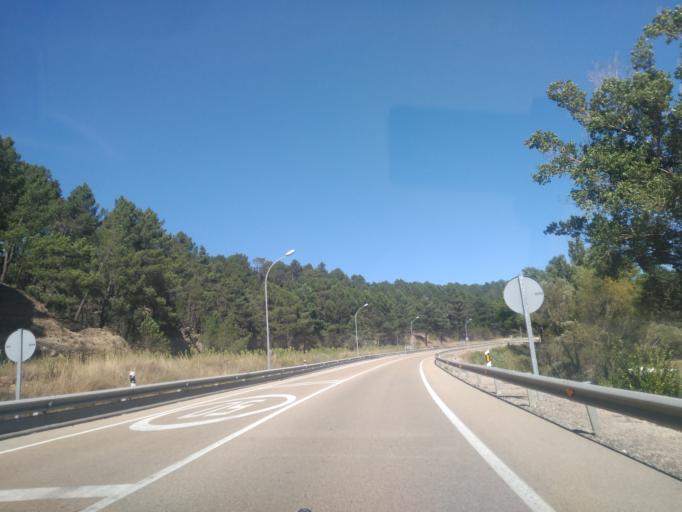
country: ES
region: Castille and Leon
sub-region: Provincia de Soria
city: San Leonardo de Yague
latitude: 41.8322
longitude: -3.0554
